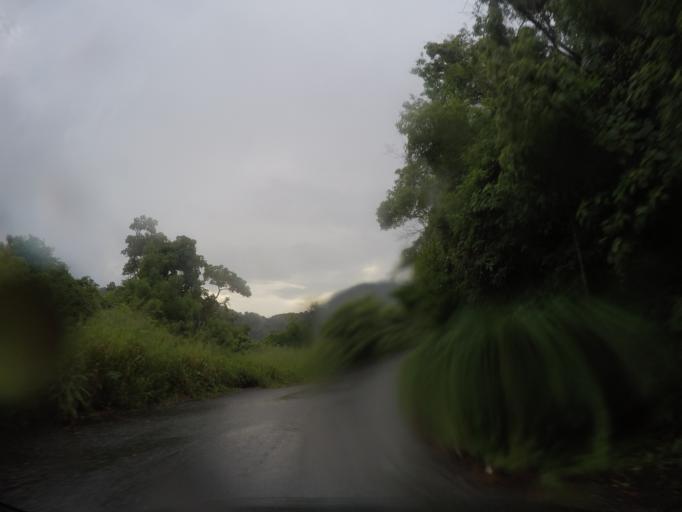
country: MX
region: Oaxaca
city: San Gabriel Mixtepec
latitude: 16.0578
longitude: -97.0764
